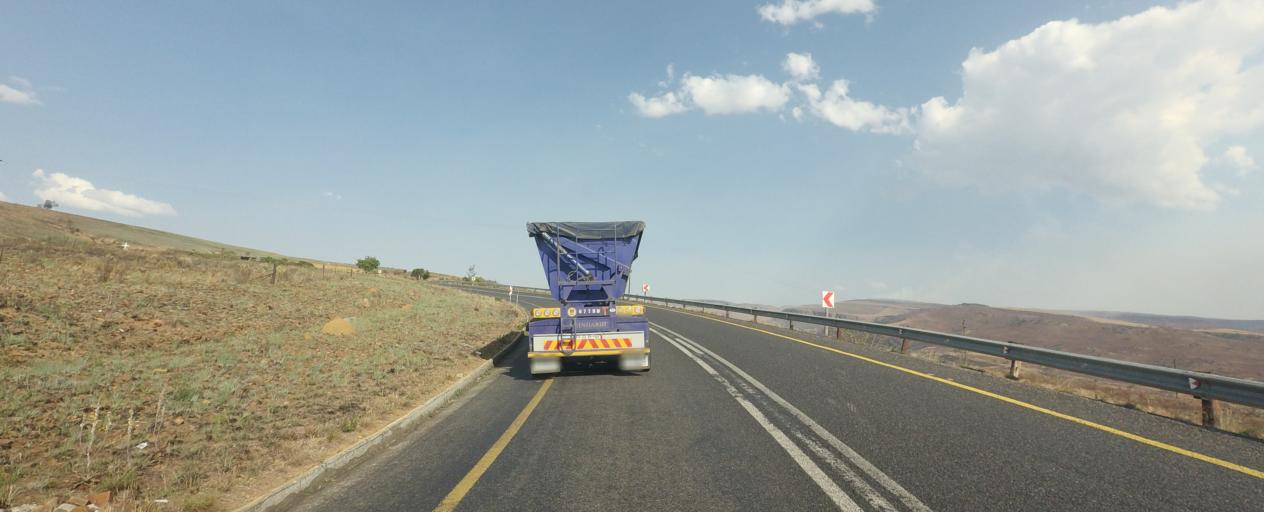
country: ZA
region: Mpumalanga
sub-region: Ehlanzeni District
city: Lydenburg
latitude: -25.1113
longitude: 30.4990
